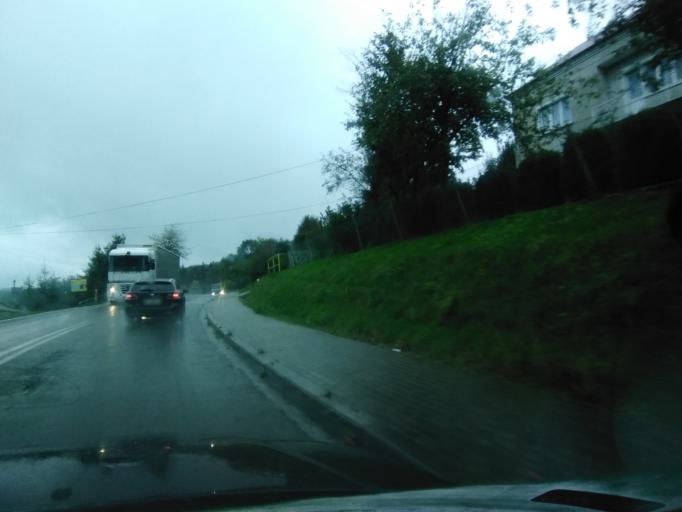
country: PL
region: Subcarpathian Voivodeship
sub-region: Powiat ropczycko-sedziszowski
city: Niedzwiada
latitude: 50.0123
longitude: 21.5521
